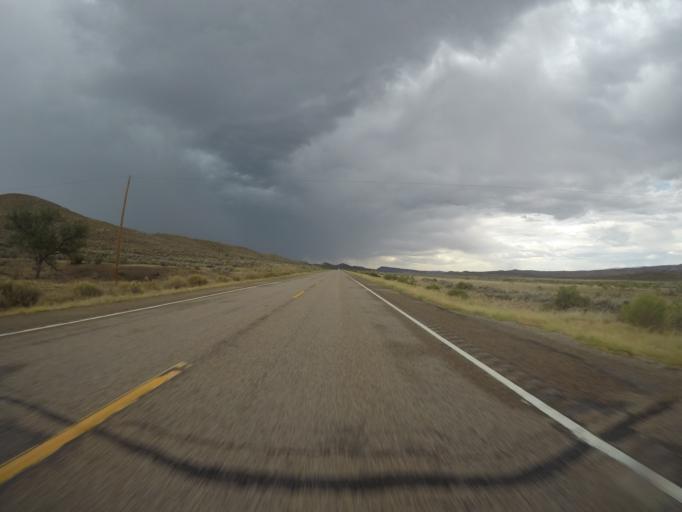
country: US
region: Colorado
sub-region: Rio Blanco County
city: Rangely
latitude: 40.2409
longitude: -108.8954
